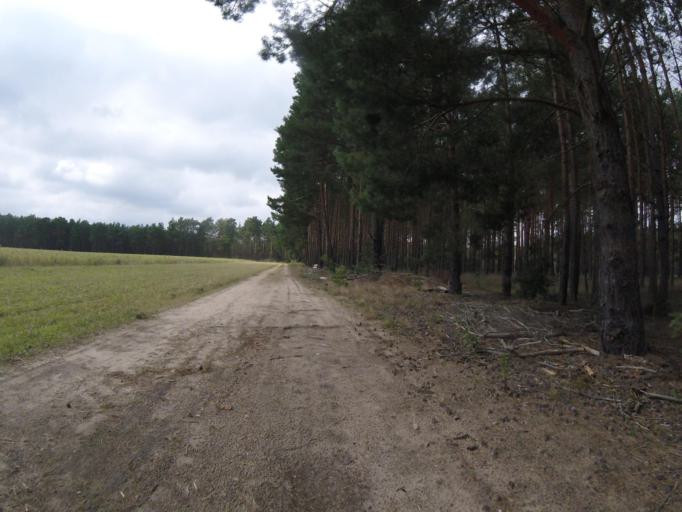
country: DE
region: Brandenburg
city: Bestensee
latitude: 52.2158
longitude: 13.6721
